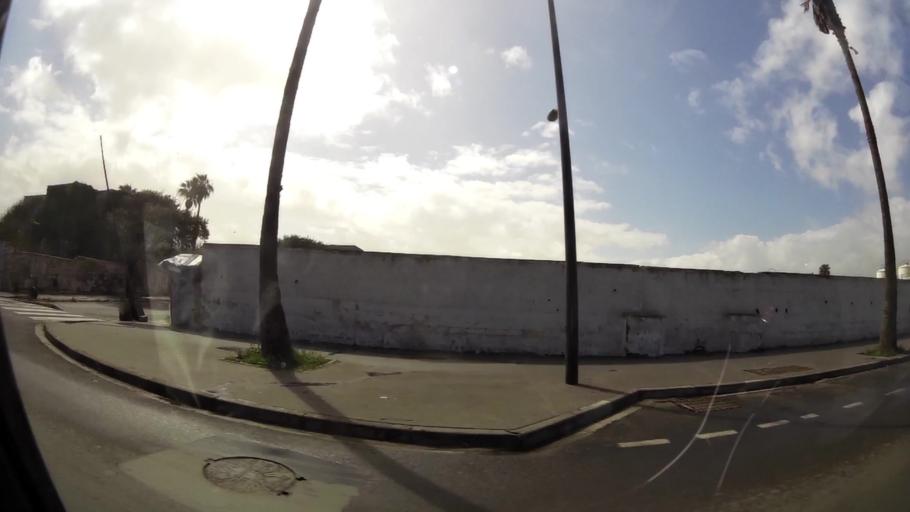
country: MA
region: Grand Casablanca
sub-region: Casablanca
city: Casablanca
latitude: 33.6167
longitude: -7.5490
